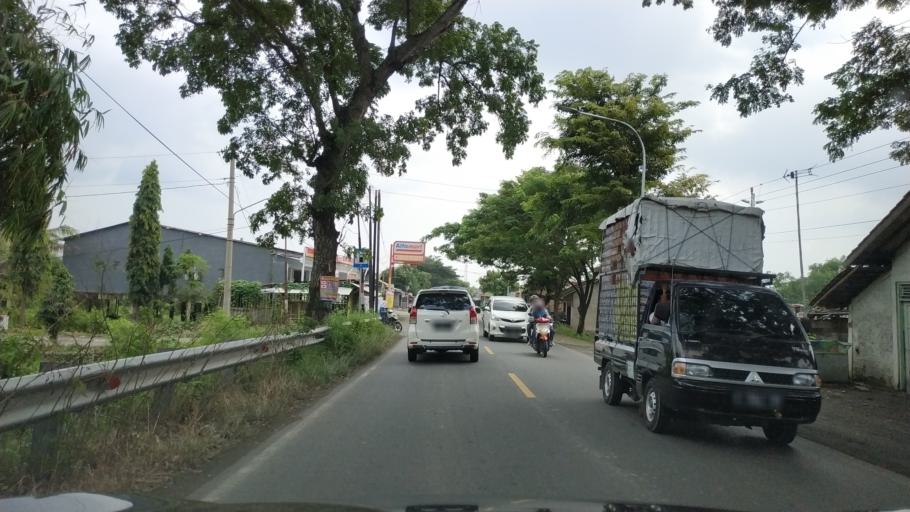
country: ID
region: Central Java
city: Slawi
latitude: -7.0149
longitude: 109.1419
